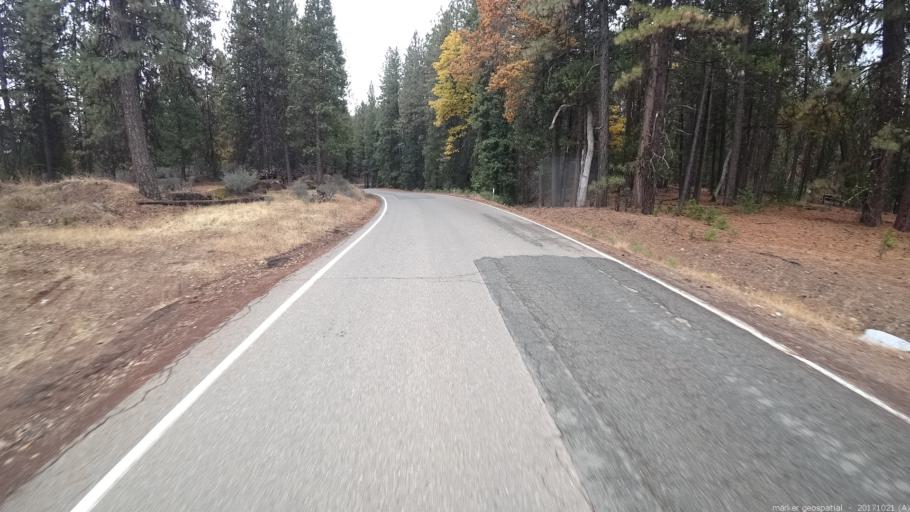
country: US
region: California
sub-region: Shasta County
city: Burney
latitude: 41.0292
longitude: -121.6719
